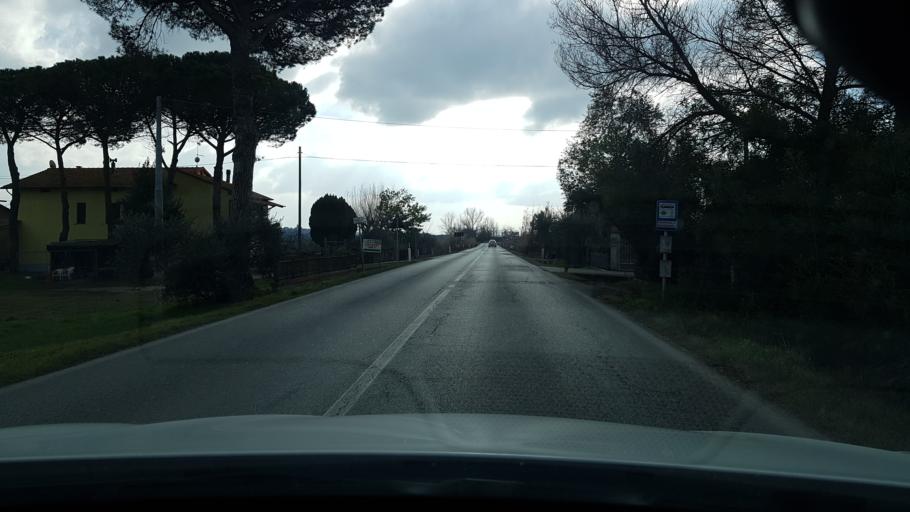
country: IT
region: Umbria
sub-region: Provincia di Perugia
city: Castiglione del Lago
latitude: 43.1475
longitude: 12.0233
